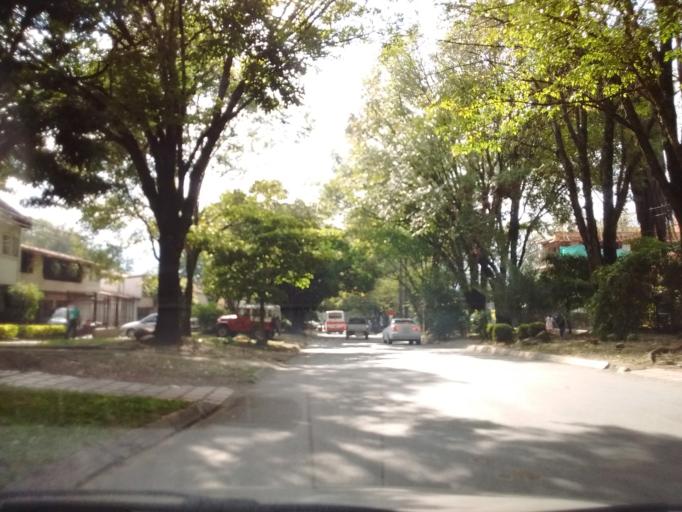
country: CO
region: Antioquia
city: Itagui
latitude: 6.2294
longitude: -75.6038
